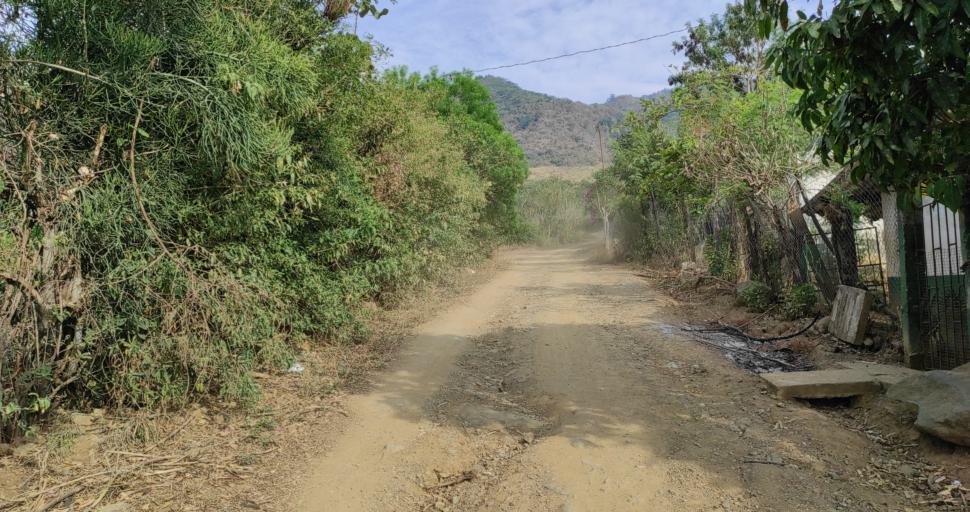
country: EC
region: Loja
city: Catacocha
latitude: -3.9916
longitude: -79.6983
